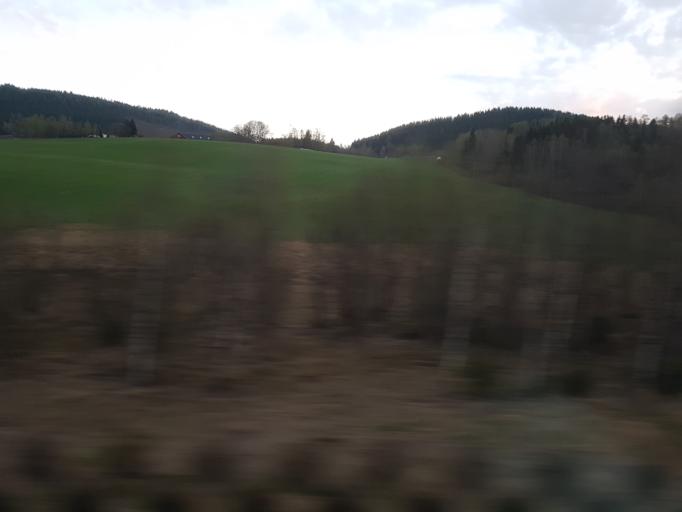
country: NO
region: Hedmark
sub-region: Ringsaker
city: Moelv
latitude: 60.9157
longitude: 10.7842
